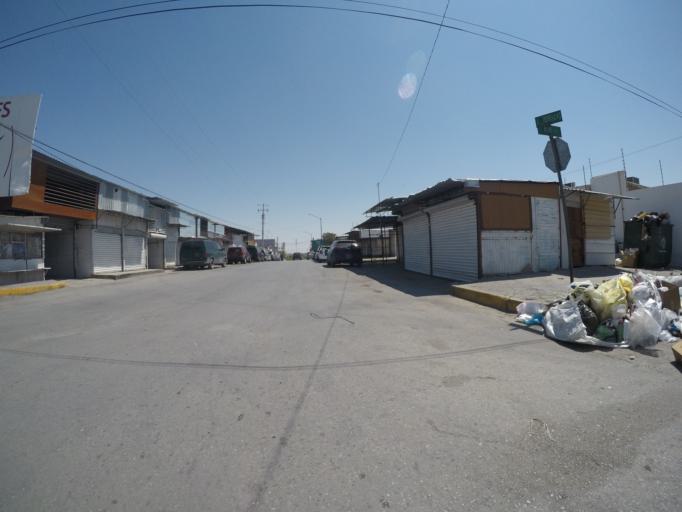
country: MX
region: Chihuahua
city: Ciudad Juarez
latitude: 31.7342
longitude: -106.4885
